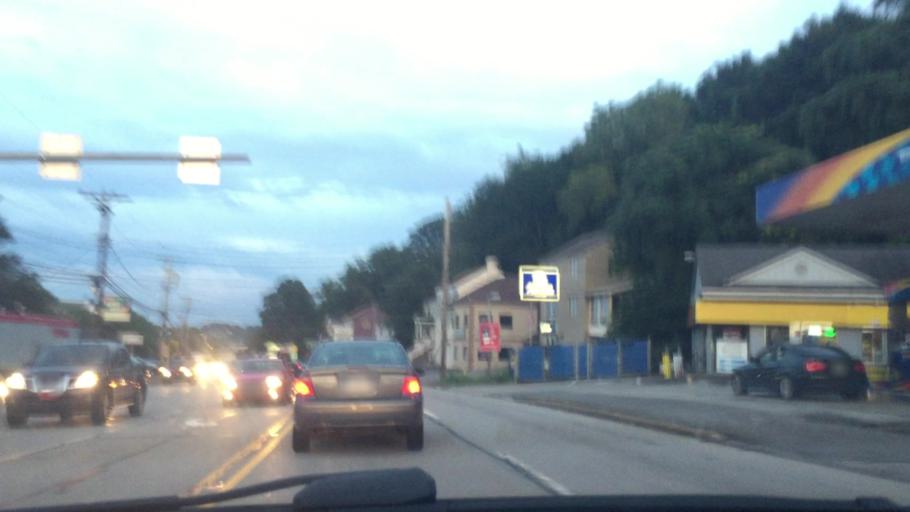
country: US
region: Pennsylvania
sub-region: Allegheny County
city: Pleasant Hills
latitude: 40.3389
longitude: -79.9601
